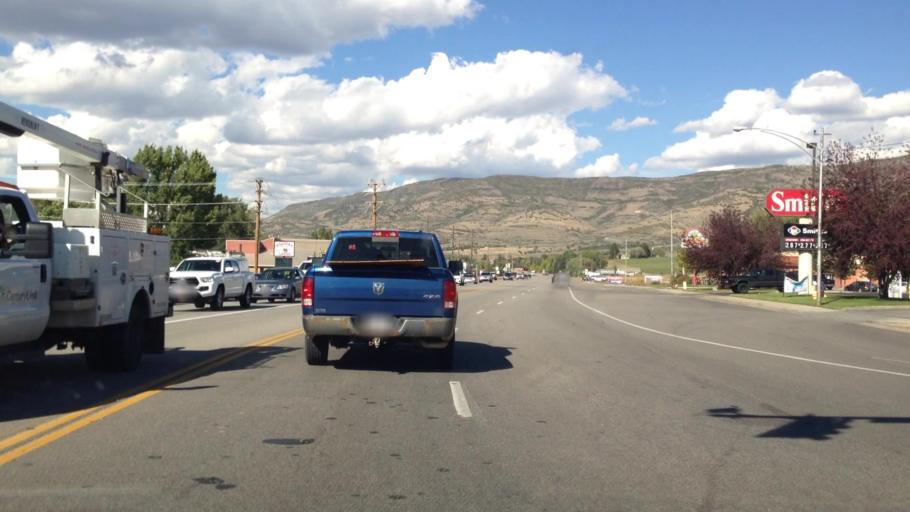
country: US
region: Utah
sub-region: Wasatch County
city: Heber
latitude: 40.5145
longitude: -111.4130
